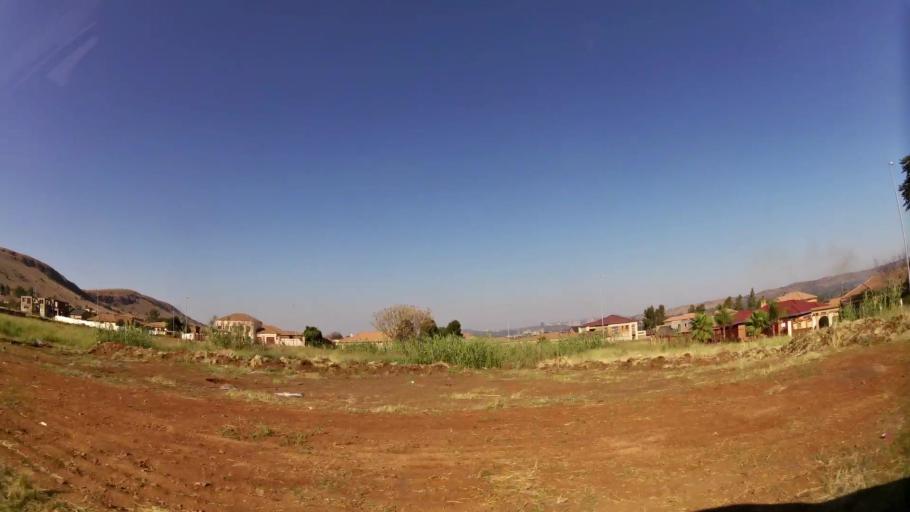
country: ZA
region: Gauteng
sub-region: City of Tshwane Metropolitan Municipality
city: Pretoria
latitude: -25.6941
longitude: 28.1312
